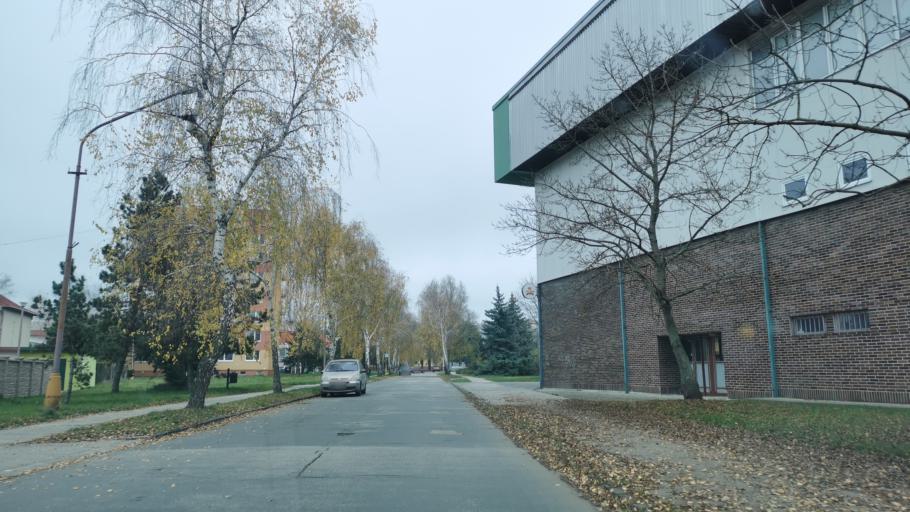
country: SK
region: Trnavsky
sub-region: Okres Skalica
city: Skalica
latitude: 48.8409
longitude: 17.2249
